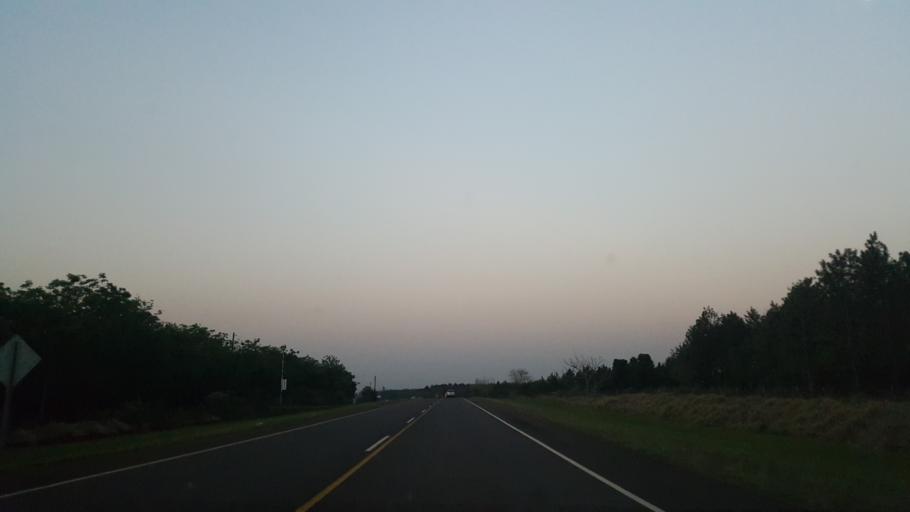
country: AR
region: Misiones
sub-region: Departamento de Capital
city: Posadas
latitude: -27.4365
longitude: -56.0156
